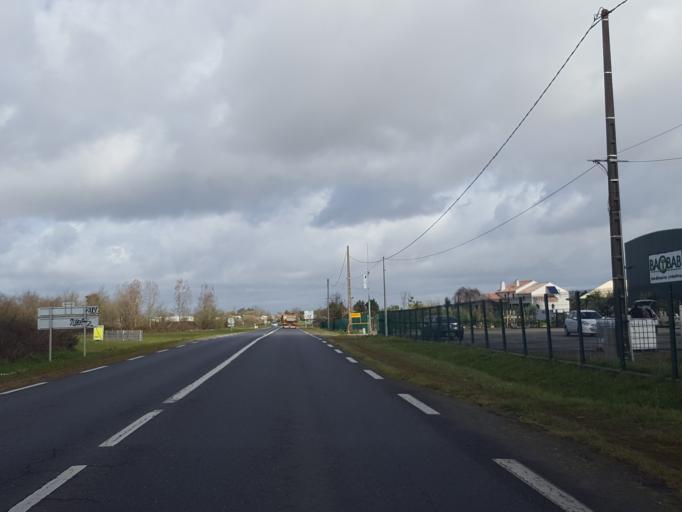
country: FR
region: Pays de la Loire
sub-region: Departement de la Loire-Atlantique
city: Les Sorinieres
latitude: 47.1071
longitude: -1.5373
